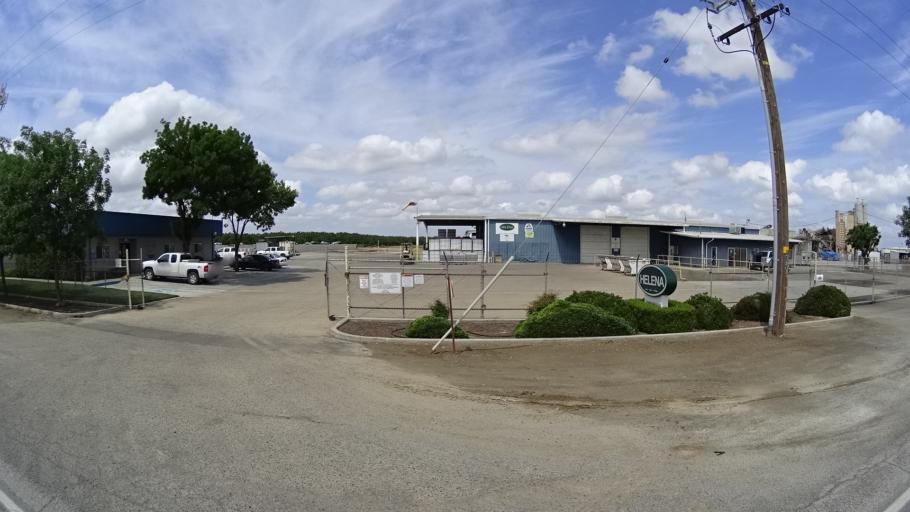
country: US
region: California
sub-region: Kings County
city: Home Garden
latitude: 36.2951
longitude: -119.6549
